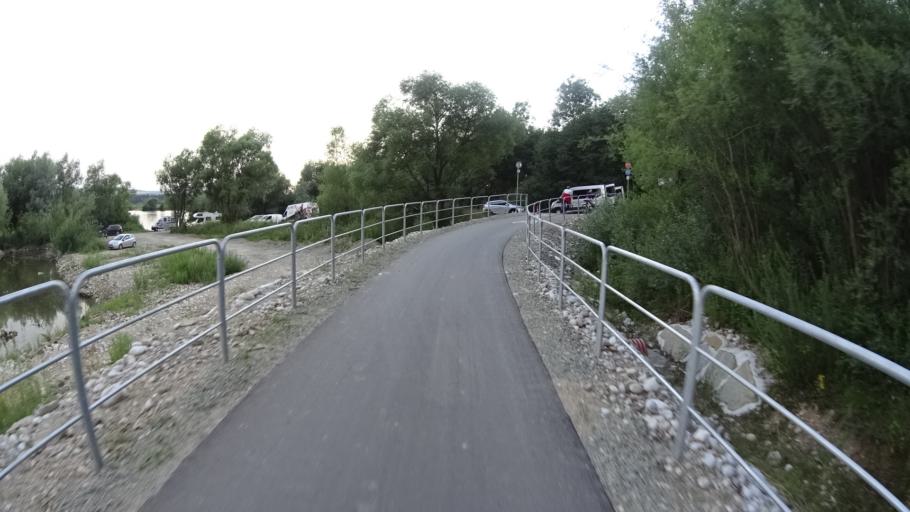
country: PL
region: Lesser Poland Voivodeship
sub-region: Powiat nowotarski
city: Frydman
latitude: 49.4664
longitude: 20.2272
